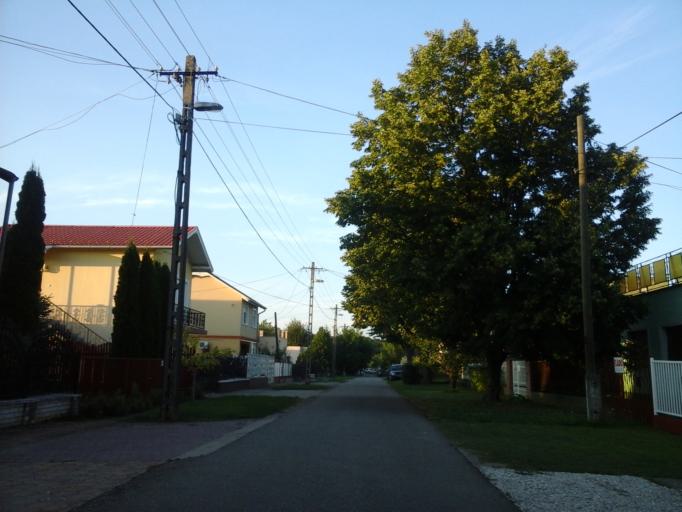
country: HU
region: Hajdu-Bihar
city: Hajduszoboszlo
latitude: 47.4588
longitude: 21.4046
